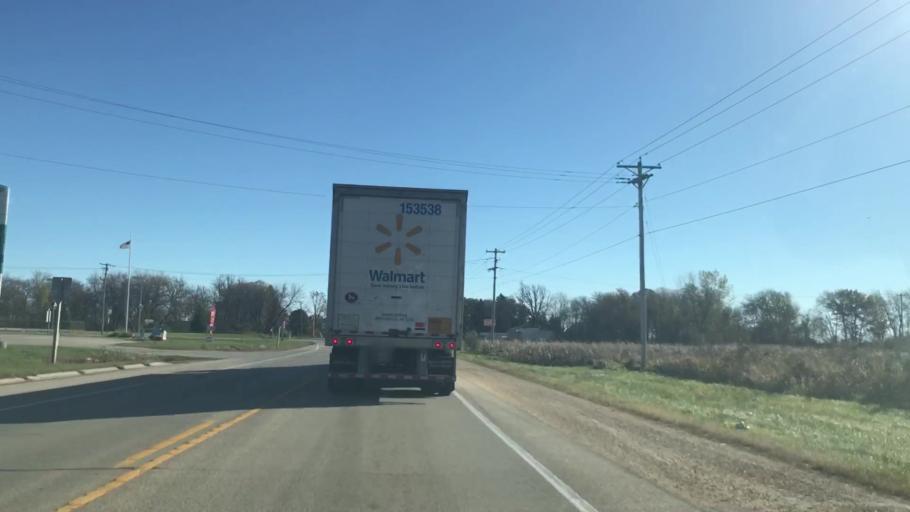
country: US
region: Wisconsin
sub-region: Dodge County
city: Juneau
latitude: 43.4449
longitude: -88.6985
